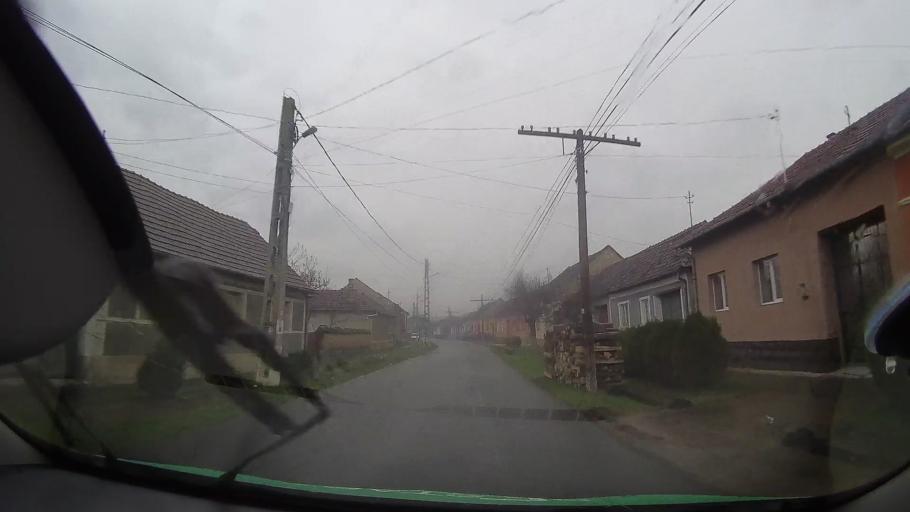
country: RO
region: Bihor
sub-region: Comuna Uileacu de Beius
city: Uileacu de Beius
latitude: 46.6824
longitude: 22.2239
